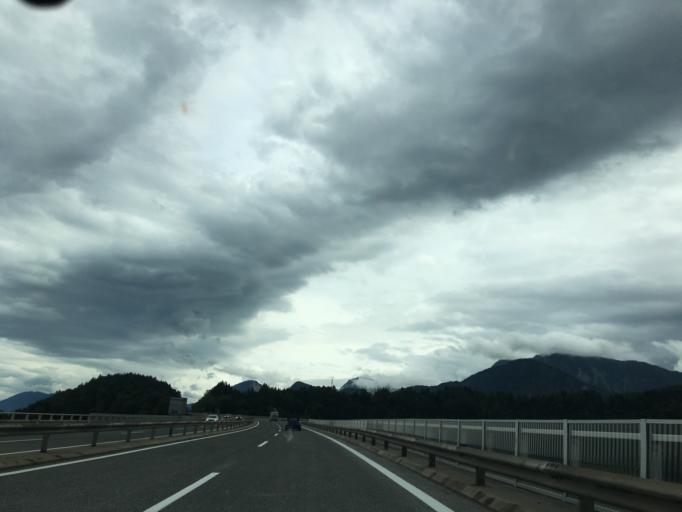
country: AT
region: Carinthia
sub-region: Politischer Bezirk Villach Land
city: Rosegg
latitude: 46.5506
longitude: 14.0105
